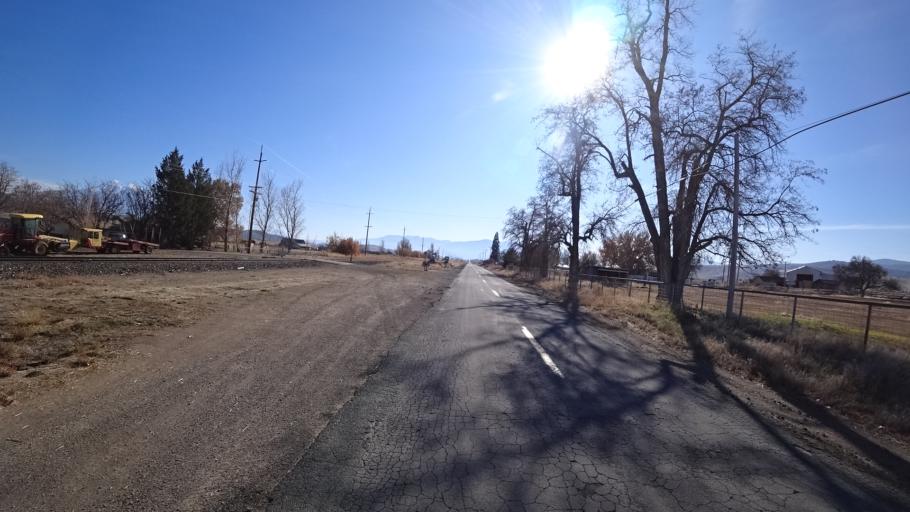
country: US
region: California
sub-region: Siskiyou County
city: Montague
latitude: 41.6213
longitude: -122.5225
